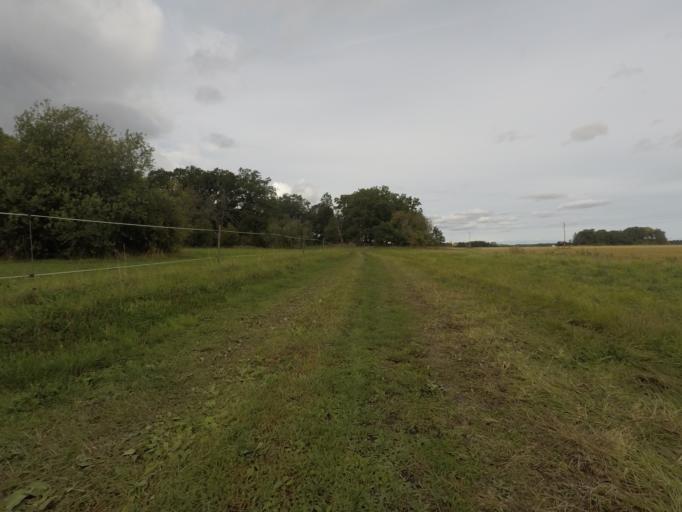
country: SE
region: Vaestmanland
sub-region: Kungsors Kommun
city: Kungsoer
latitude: 59.4546
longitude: 16.0504
